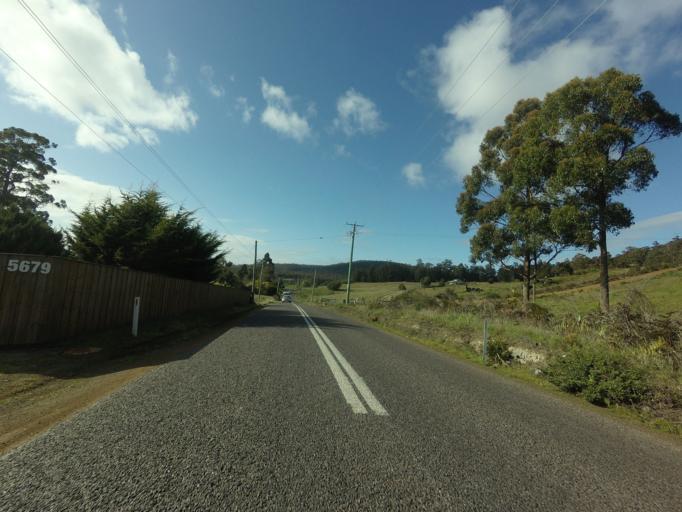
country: AU
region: Tasmania
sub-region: Huon Valley
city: Geeveston
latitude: -43.2112
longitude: 146.9854
